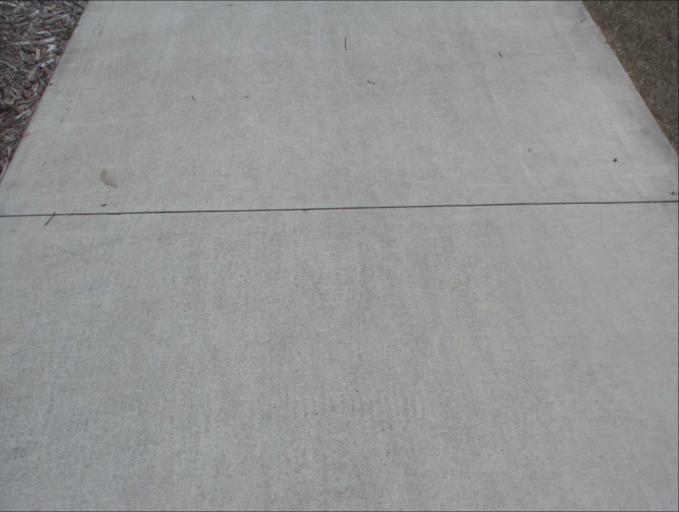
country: AU
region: Queensland
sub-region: Logan
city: North Maclean
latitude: -27.8098
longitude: 152.9578
